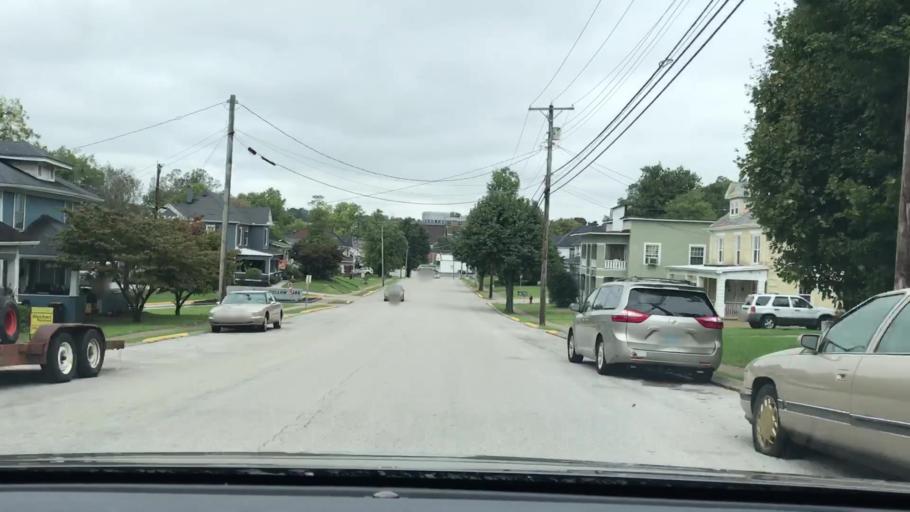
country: US
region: Kentucky
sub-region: Pulaski County
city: Somerset
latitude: 37.0888
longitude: -84.5998
